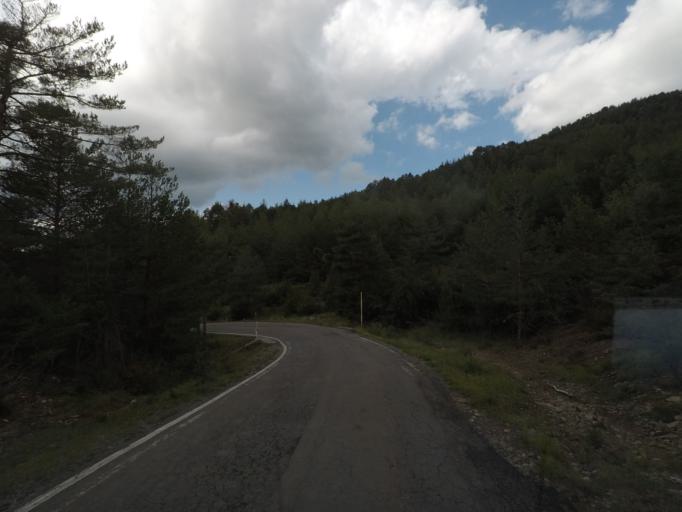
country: ES
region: Aragon
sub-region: Provincia de Huesca
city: Fiscal
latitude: 42.4094
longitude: -0.1014
